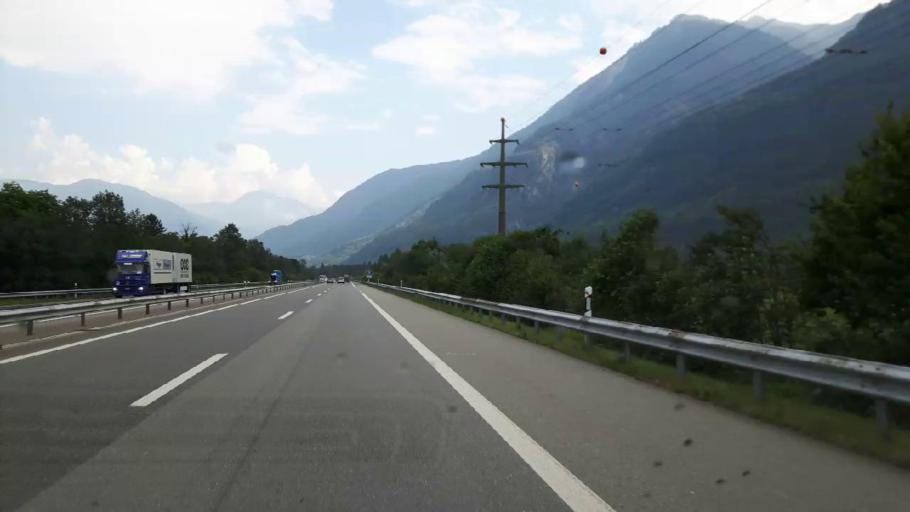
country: CH
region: Ticino
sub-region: Riviera District
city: Lodrino
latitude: 46.2870
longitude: 8.9920
